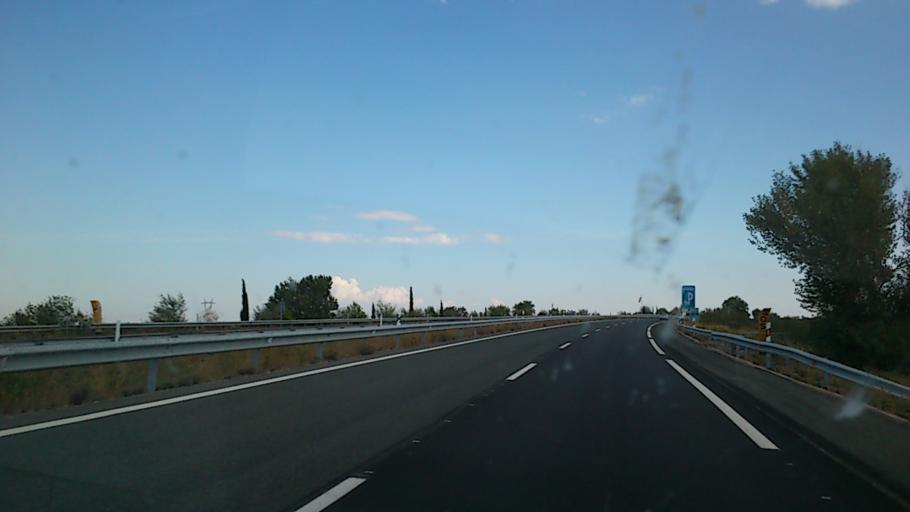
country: ES
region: Navarre
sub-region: Provincia de Navarra
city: Corella
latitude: 42.1227
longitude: -1.7474
